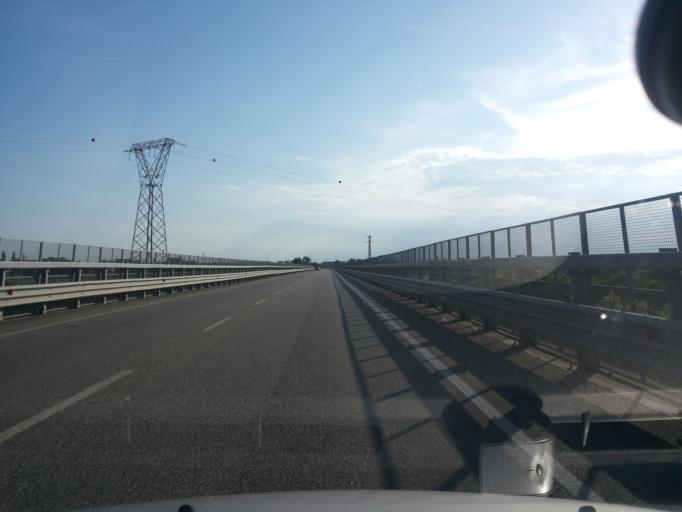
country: IT
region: Piedmont
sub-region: Provincia di Vercelli
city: Vercelli
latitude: 45.3432
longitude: 8.4352
